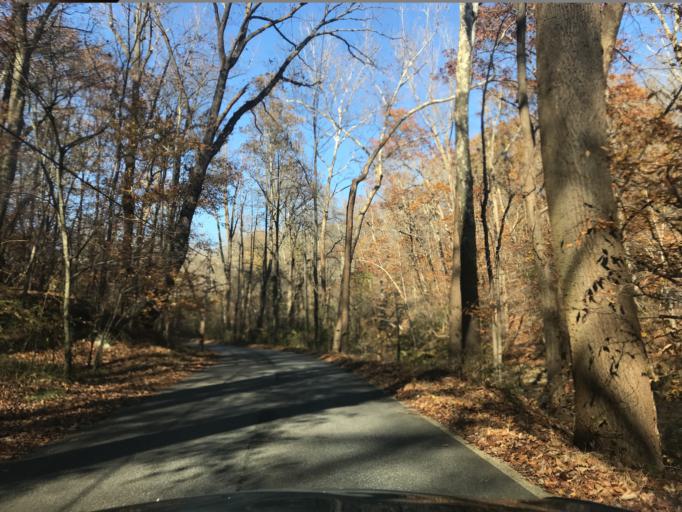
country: US
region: Maryland
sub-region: Baltimore County
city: Perry Hall
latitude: 39.4497
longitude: -76.4736
